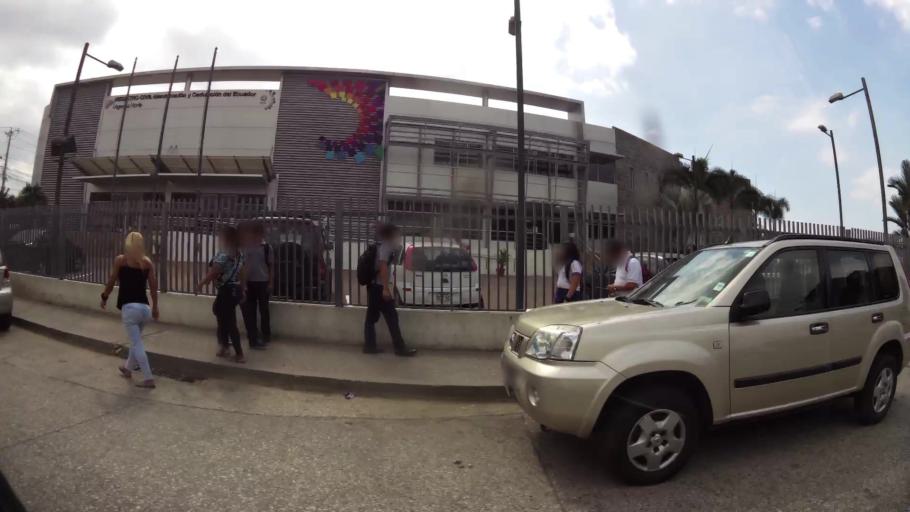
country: EC
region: Guayas
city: Santa Lucia
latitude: -2.1008
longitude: -79.9403
